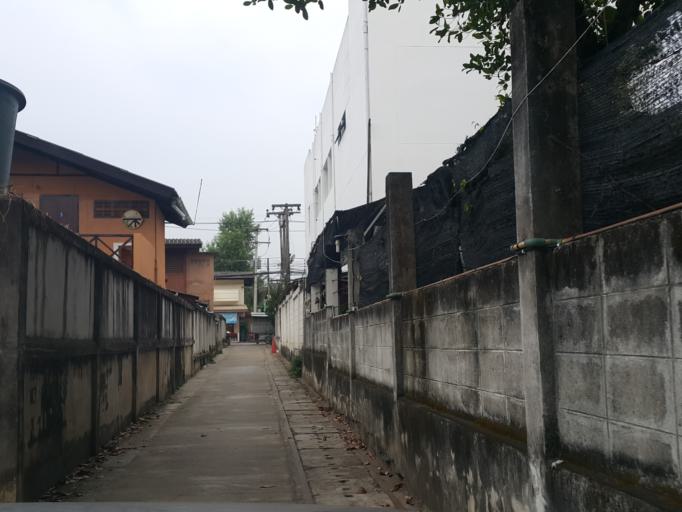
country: TH
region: Chiang Mai
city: Pai
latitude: 19.3591
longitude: 98.4417
